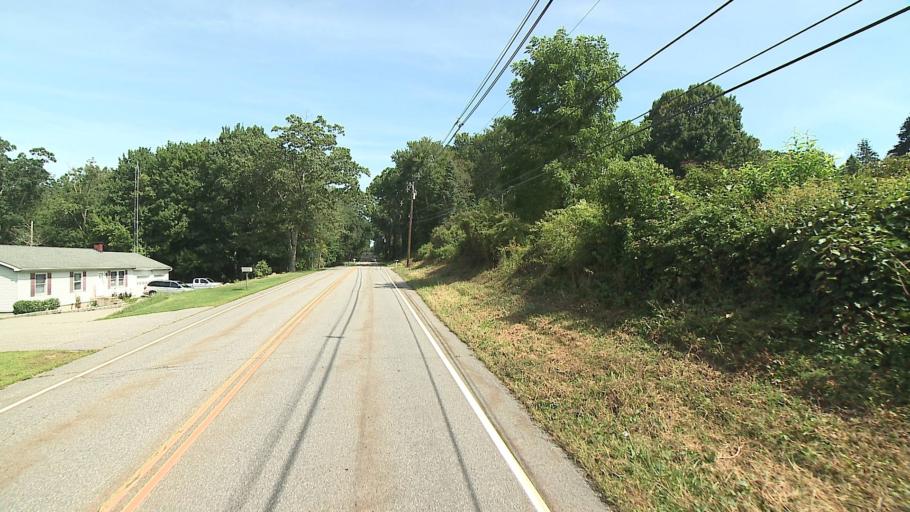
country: US
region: Connecticut
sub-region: Litchfield County
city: Bethlehem Village
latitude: 41.6537
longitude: -73.2013
